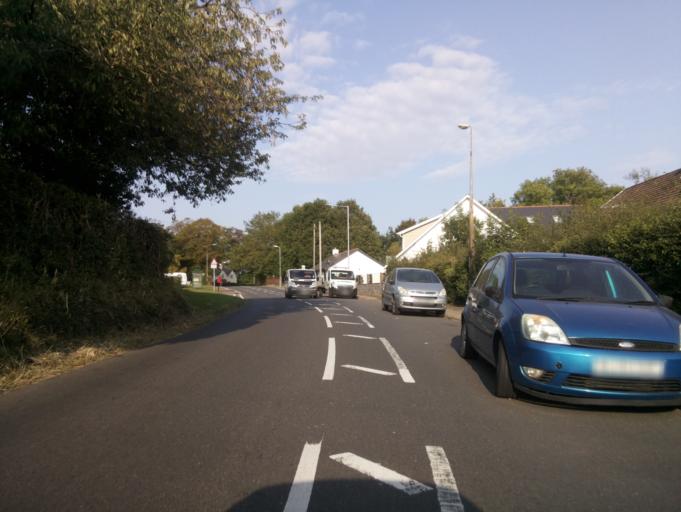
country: GB
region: Wales
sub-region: Torfaen County Borough
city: Cwmbran
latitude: 51.6655
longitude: -3.0323
